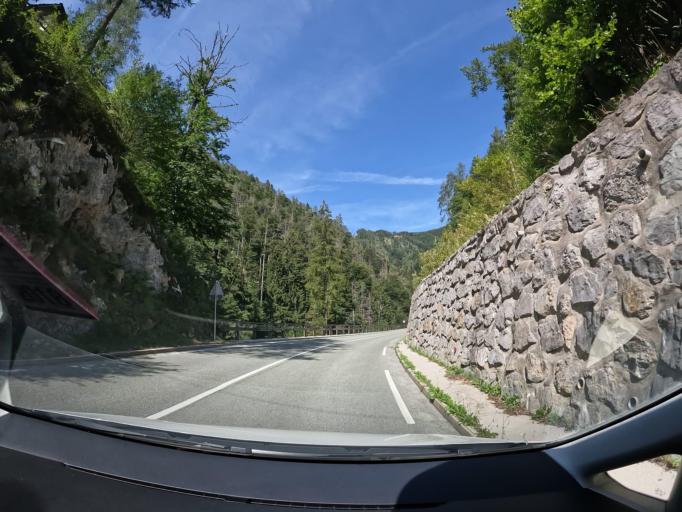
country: SI
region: Trzic
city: Trzic
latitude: 46.4148
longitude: 14.2948
